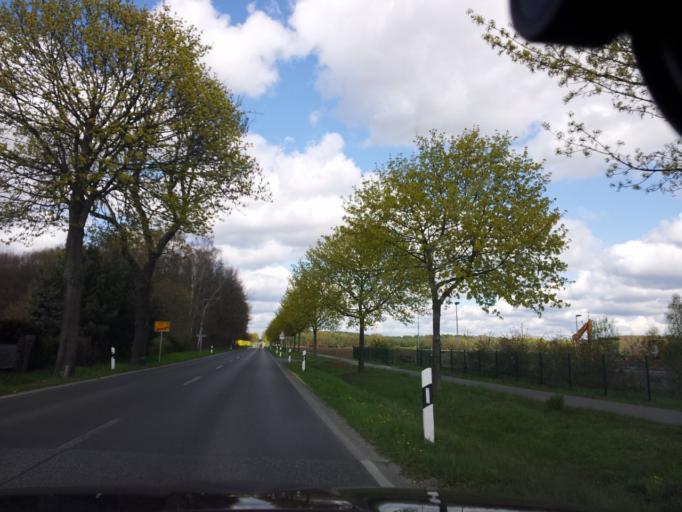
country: DE
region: Brandenburg
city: Bernau bei Berlin
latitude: 52.6895
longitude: 13.6012
